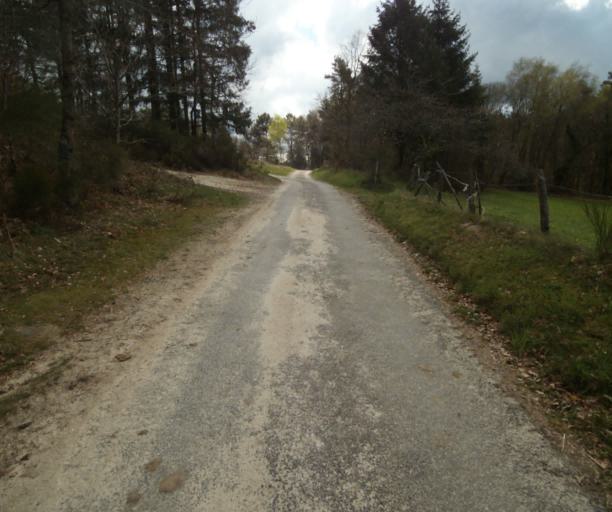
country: FR
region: Limousin
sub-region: Departement de la Correze
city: Correze
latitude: 45.2825
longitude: 1.9057
